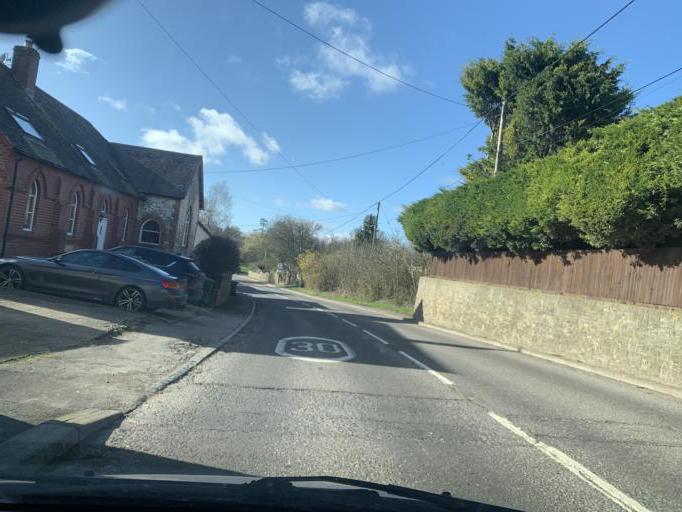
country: GB
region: England
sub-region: Wiltshire
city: Stockton
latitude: 51.1942
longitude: -2.0109
